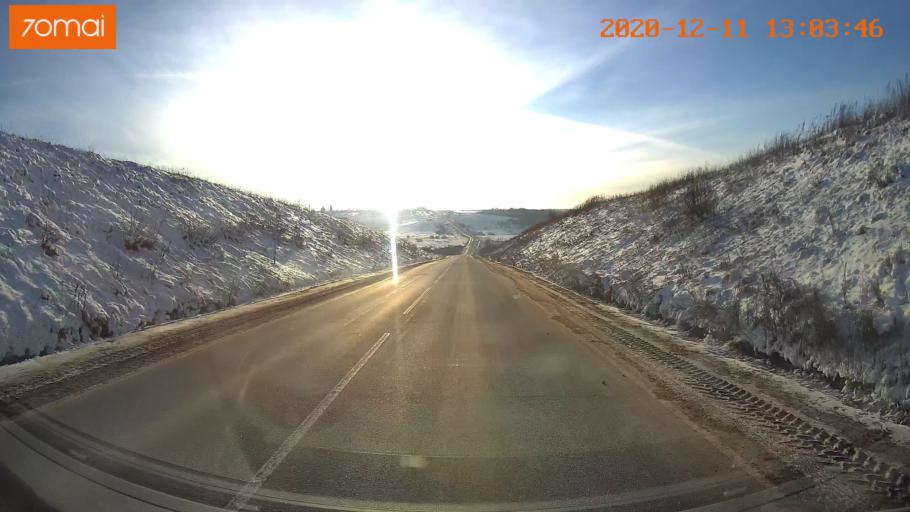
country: RU
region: Kostroma
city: Chistyye Bory
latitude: 58.2659
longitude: 41.6723
